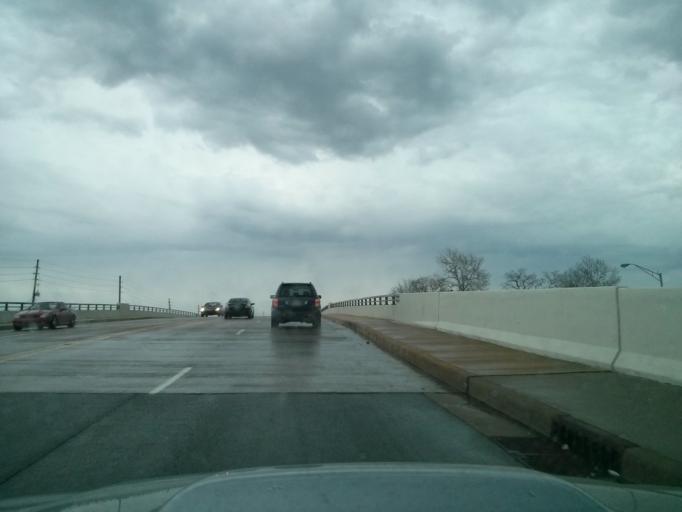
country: US
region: Indiana
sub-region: Marion County
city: Lawrence
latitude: 39.8906
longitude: -86.0518
